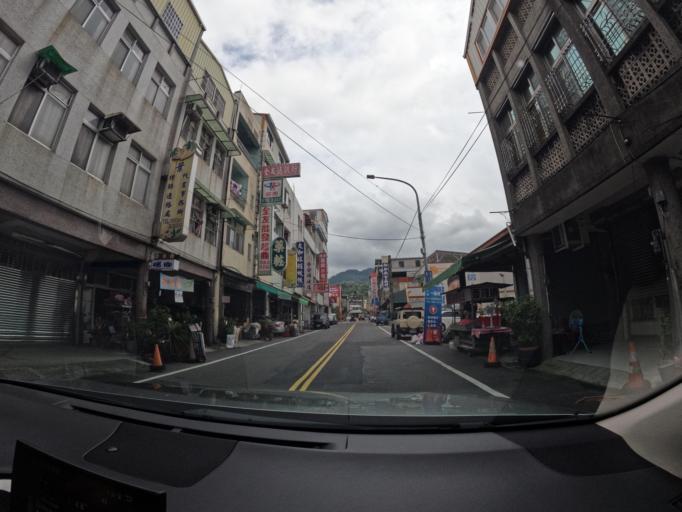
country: TW
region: Taiwan
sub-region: Miaoli
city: Miaoli
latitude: 24.4225
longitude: 120.8670
